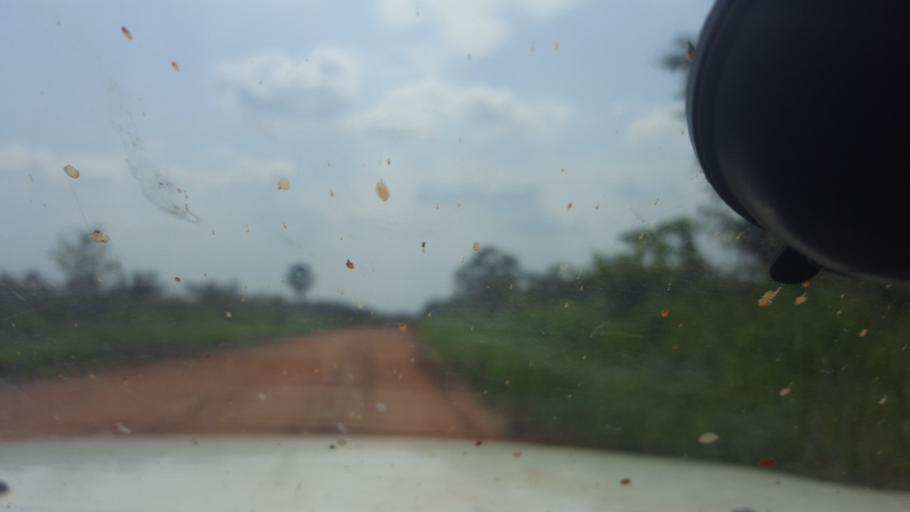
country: CD
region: Bandundu
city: Bandundu
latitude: -3.7617
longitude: 17.1368
